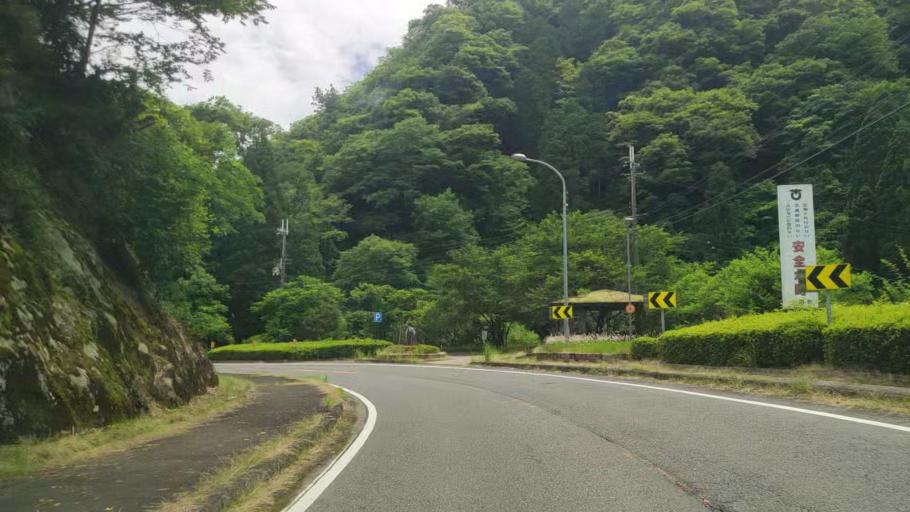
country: JP
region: Hyogo
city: Yamazakicho-nakabirose
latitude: 35.0944
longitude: 134.3609
